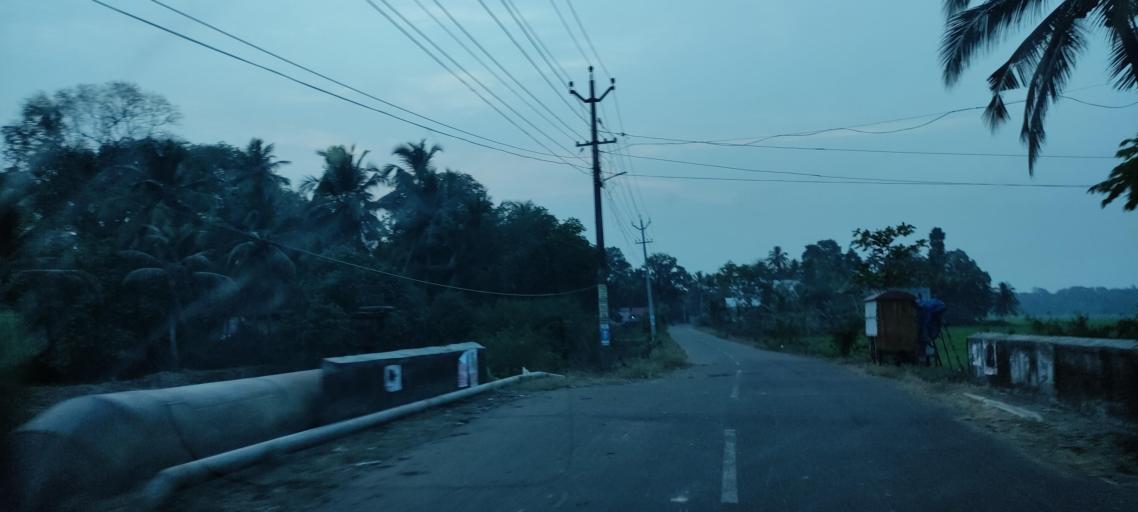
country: IN
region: Kerala
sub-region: Alappuzha
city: Mavelikara
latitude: 9.3305
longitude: 76.4970
